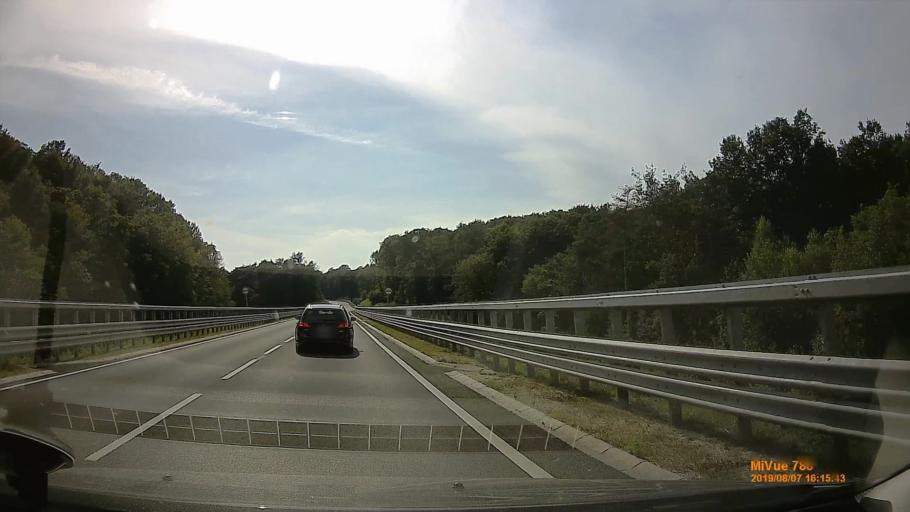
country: HU
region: Zala
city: Zalalovo
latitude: 46.8248
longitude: 16.5922
